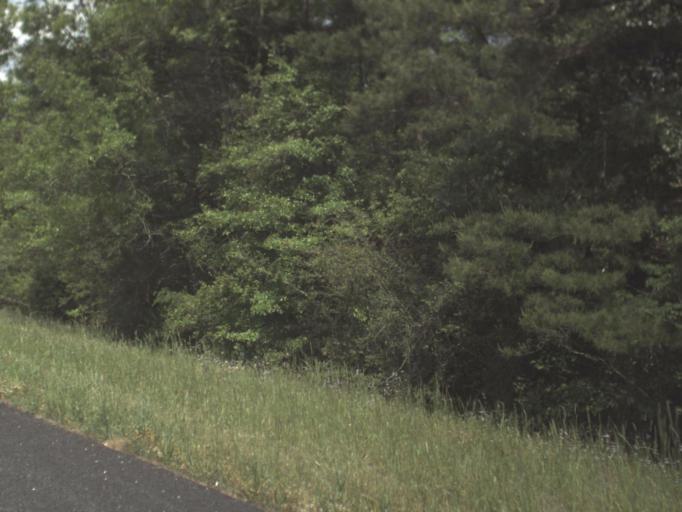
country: US
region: Florida
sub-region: Escambia County
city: Molino
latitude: 30.8476
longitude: -87.3219
